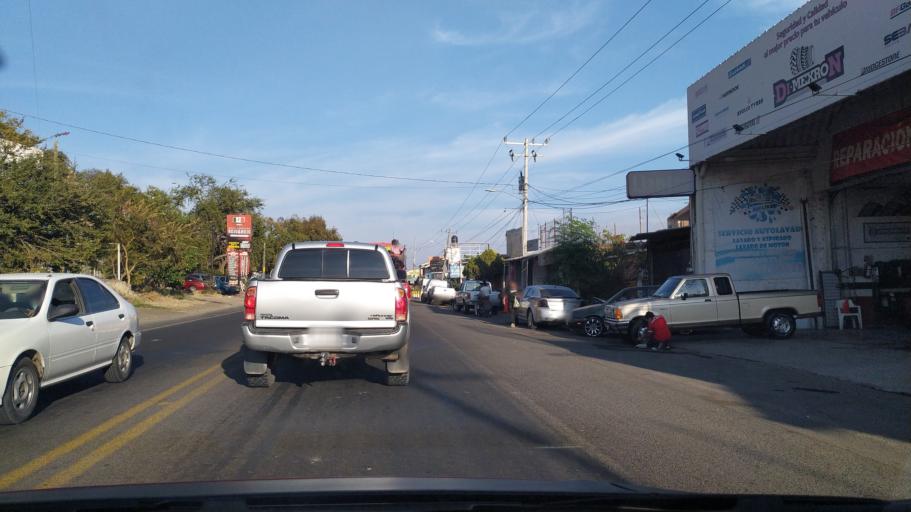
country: MX
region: Jalisco
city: Jamay
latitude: 20.2939
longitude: -102.7137
